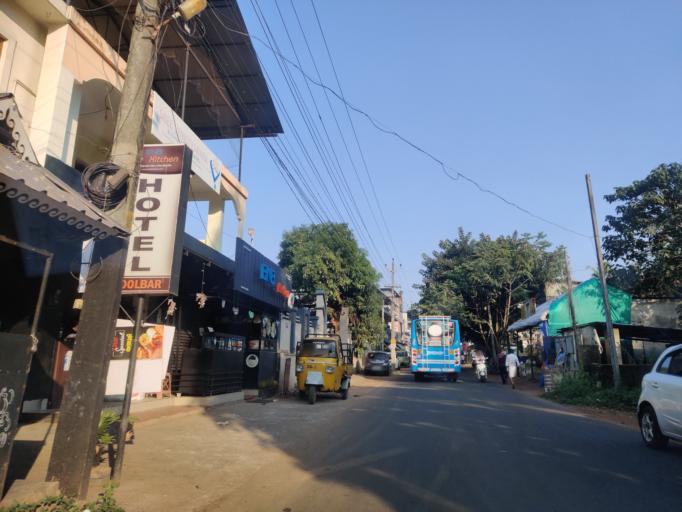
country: IN
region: Kerala
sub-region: Thrissur District
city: Kunnamkulam
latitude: 10.7349
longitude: 76.0259
